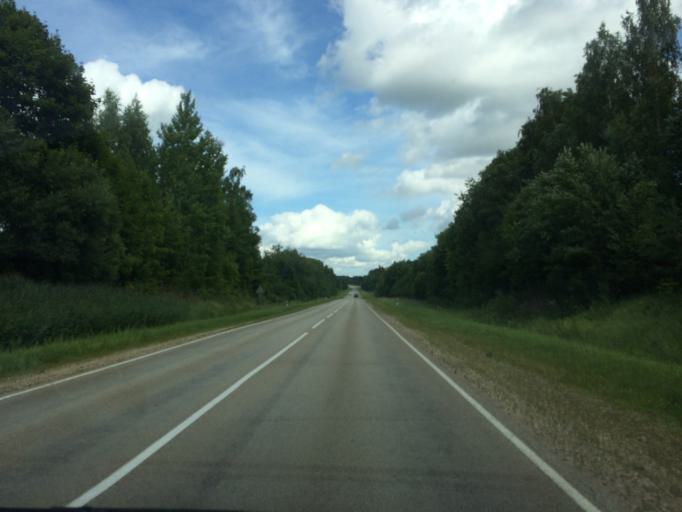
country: LV
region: Rezekne
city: Rezekne
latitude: 56.6044
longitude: 27.4316
